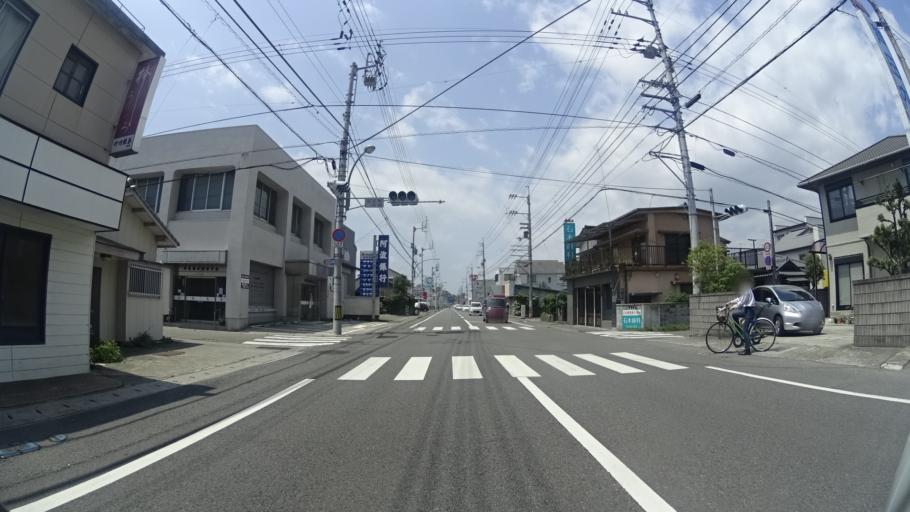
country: JP
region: Tokushima
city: Ishii
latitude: 34.0714
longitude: 134.4775
